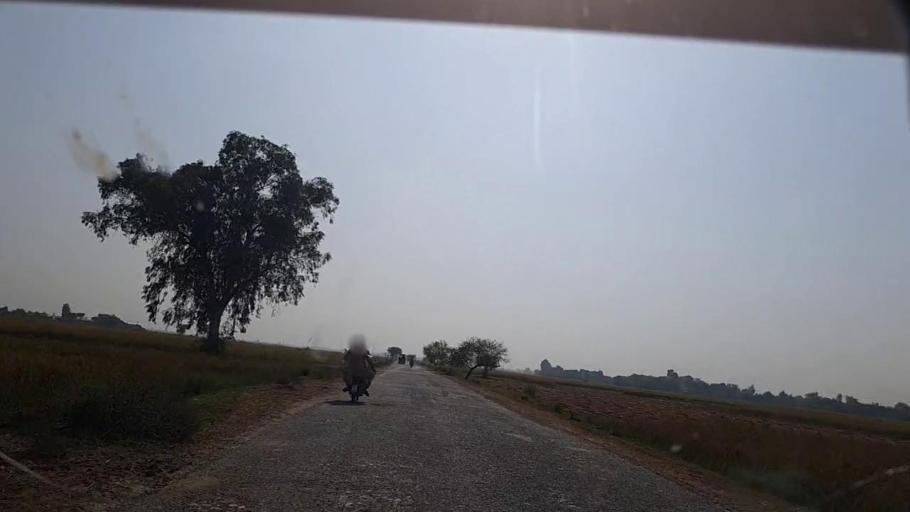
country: PK
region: Sindh
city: Shikarpur
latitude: 28.0932
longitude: 68.6086
